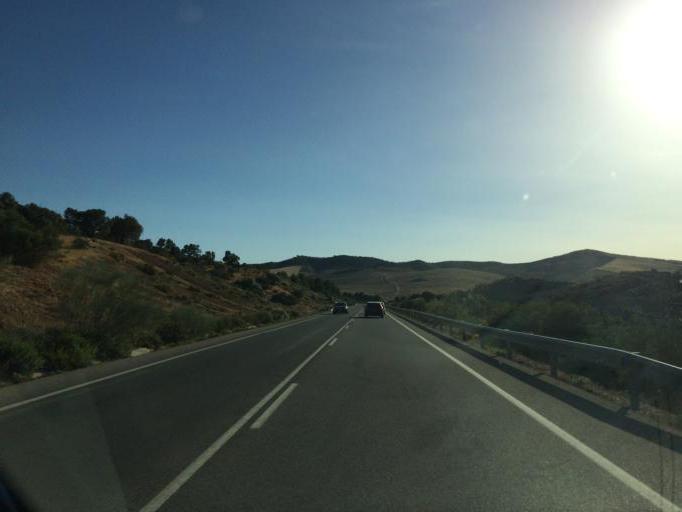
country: ES
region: Andalusia
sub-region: Provincia de Malaga
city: Teba
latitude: 36.9710
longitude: -4.8396
